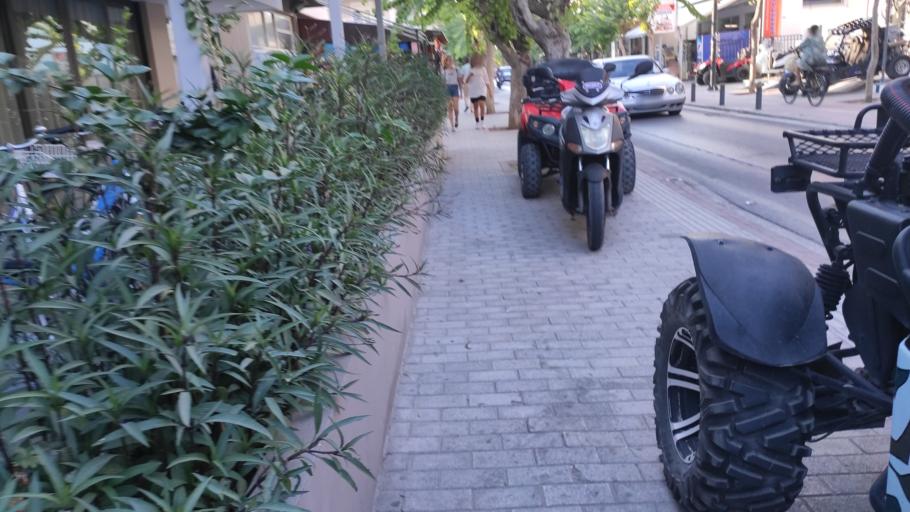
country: GR
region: South Aegean
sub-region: Nomos Dodekanisou
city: Kos
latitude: 36.8993
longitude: 27.2837
